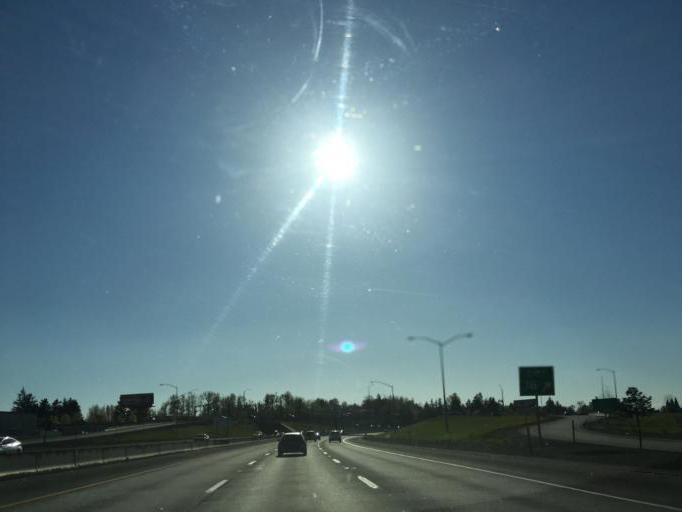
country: US
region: Oregon
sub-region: Multnomah County
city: Wood Village
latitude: 45.5409
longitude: -122.4149
